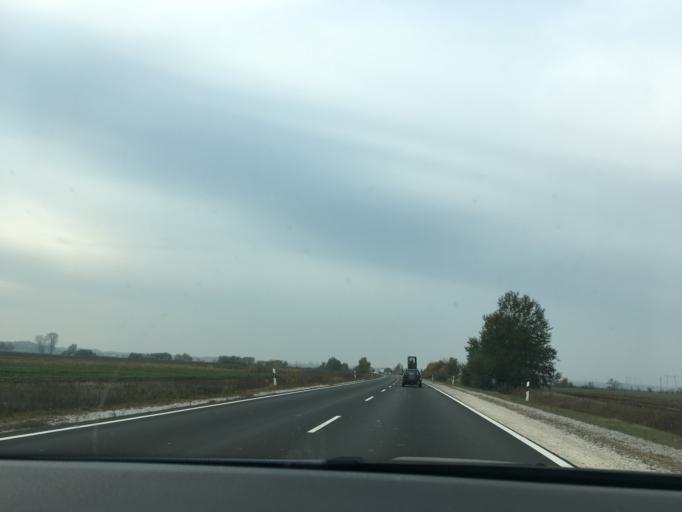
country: HU
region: Pest
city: Abony
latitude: 47.2209
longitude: 20.0090
